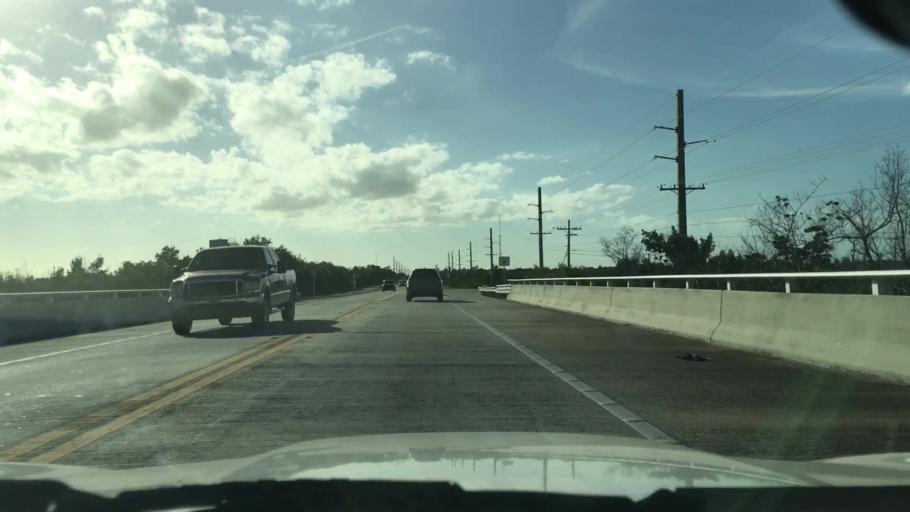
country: US
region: Florida
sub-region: Monroe County
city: Big Pine Key
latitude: 24.6643
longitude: -81.3973
